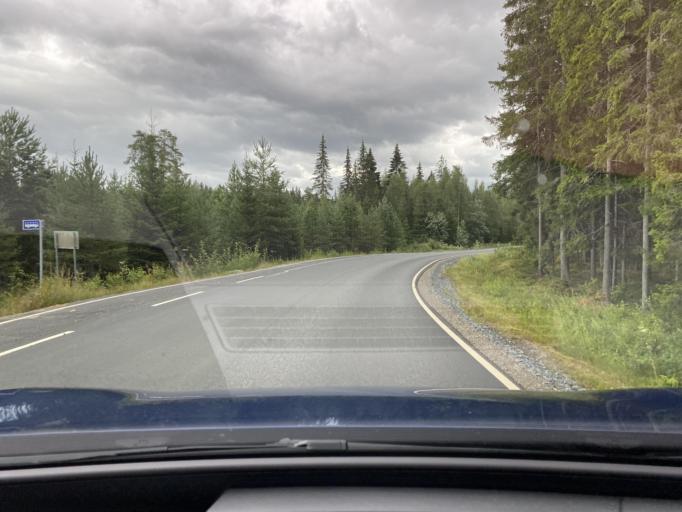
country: FI
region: Pirkanmaa
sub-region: Lounais-Pirkanmaa
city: Punkalaidun
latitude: 61.2568
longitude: 23.1113
